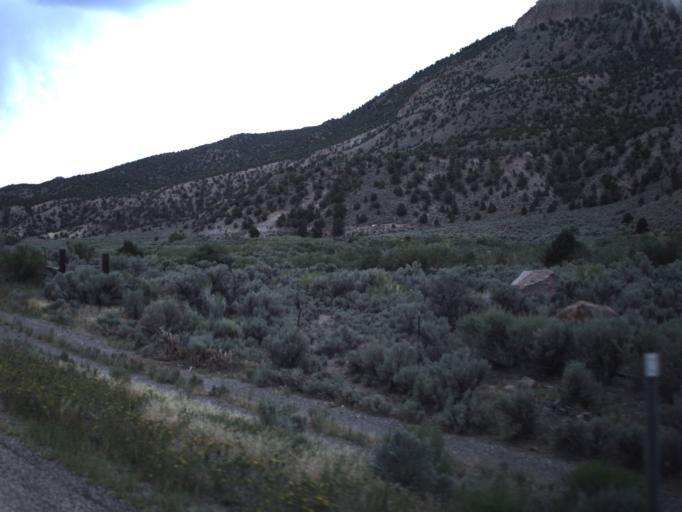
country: US
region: Utah
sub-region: Piute County
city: Junction
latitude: 38.1972
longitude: -112.1230
